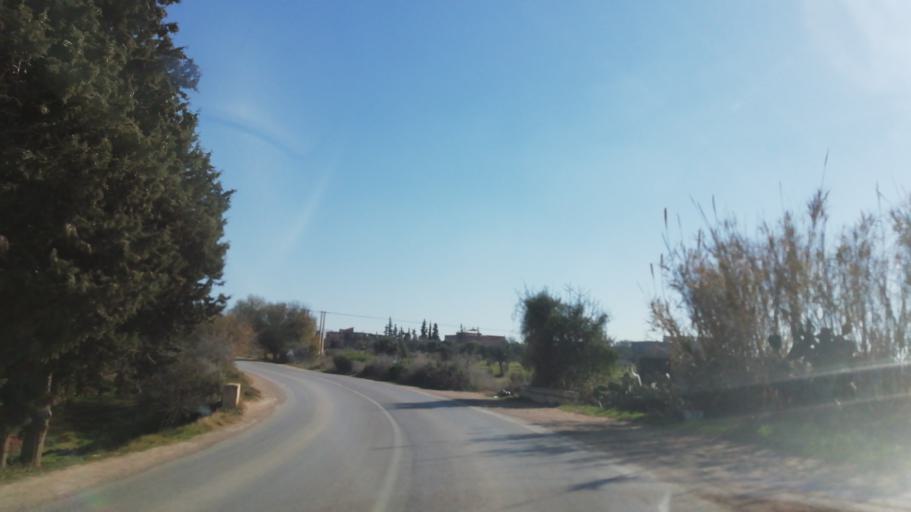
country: DZ
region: Tlemcen
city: Nedroma
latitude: 34.8319
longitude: -1.6951
